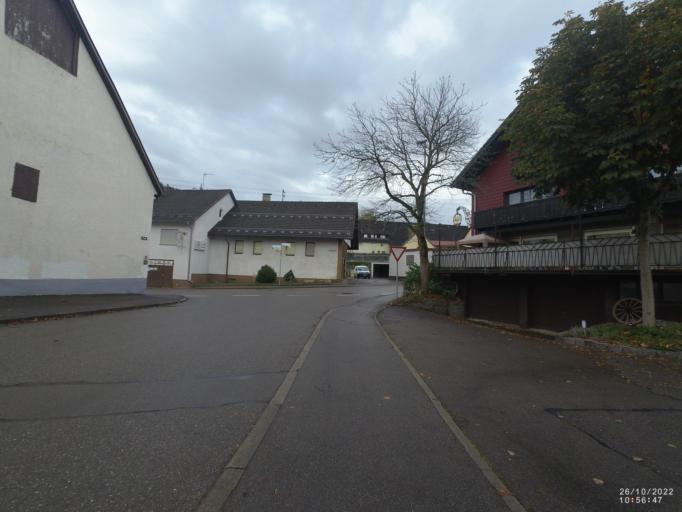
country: DE
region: Baden-Wuerttemberg
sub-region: Regierungsbezirk Stuttgart
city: Bohmenkirch
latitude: 48.6897
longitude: 9.8931
